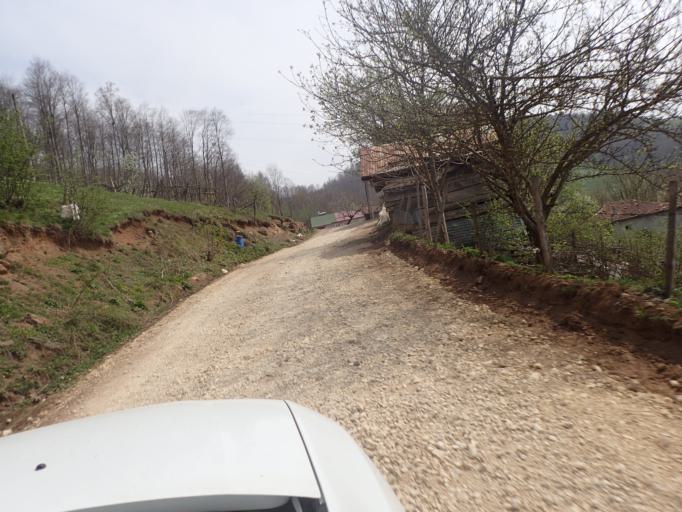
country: TR
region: Ordu
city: Aybasti
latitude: 40.7050
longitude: 37.2866
